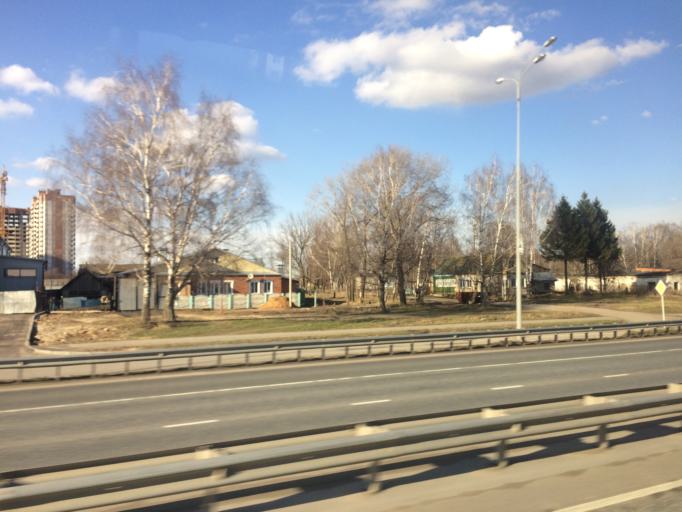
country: RU
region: Tatarstan
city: Osinovo
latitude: 55.8489
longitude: 48.9017
